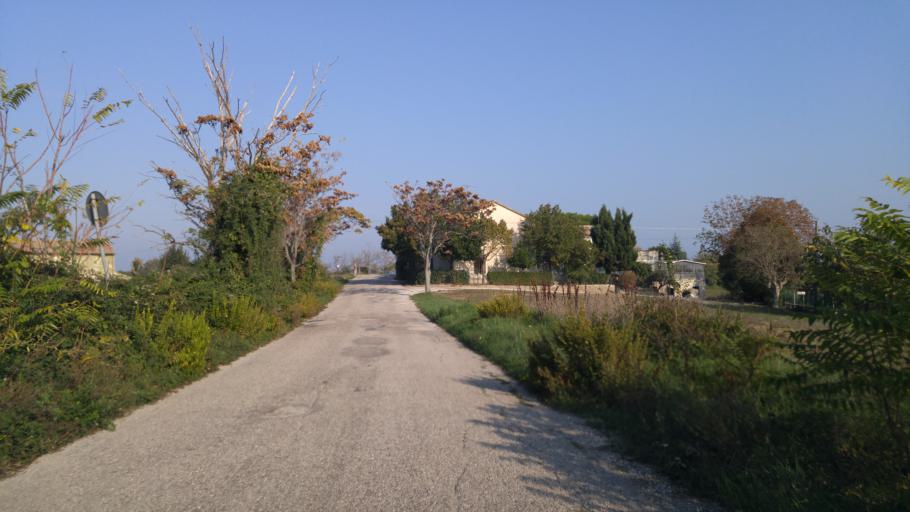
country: IT
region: The Marches
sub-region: Provincia di Pesaro e Urbino
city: Fenile
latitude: 43.8716
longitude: 12.9695
